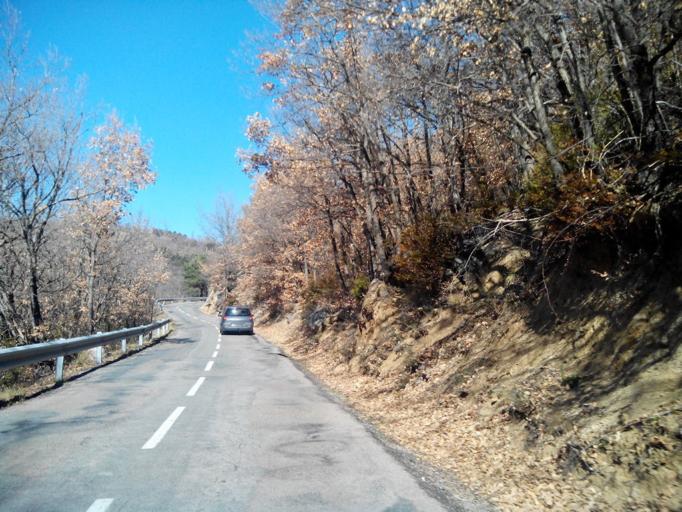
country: ES
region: Catalonia
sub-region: Provincia de Lleida
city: Lles de Cerdanya
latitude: 42.3714
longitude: 1.6842
